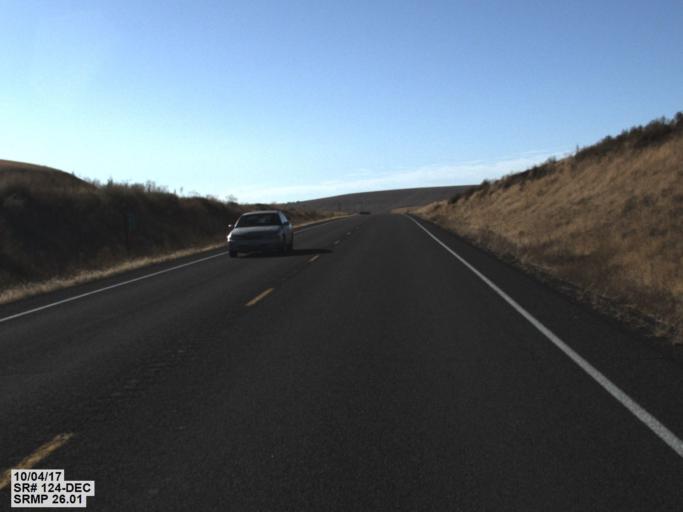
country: US
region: Washington
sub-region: Walla Walla County
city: Garrett
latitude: 46.2906
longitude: -118.5177
